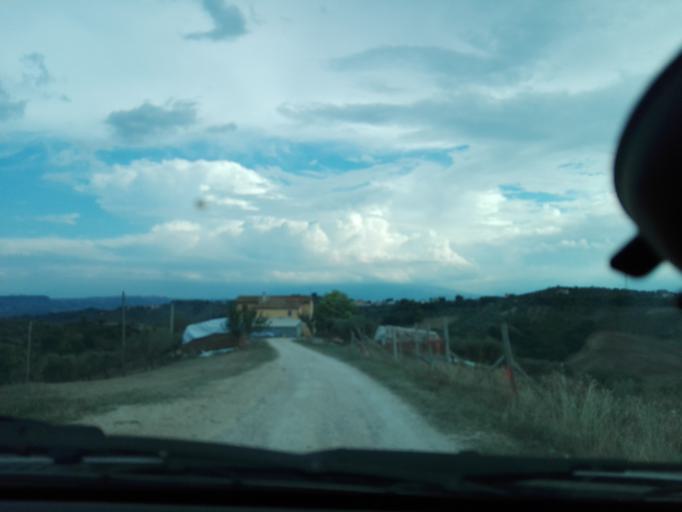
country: IT
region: Abruzzo
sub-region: Provincia di Pescara
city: Cappelle sul Tavo
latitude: 42.4493
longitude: 14.1007
